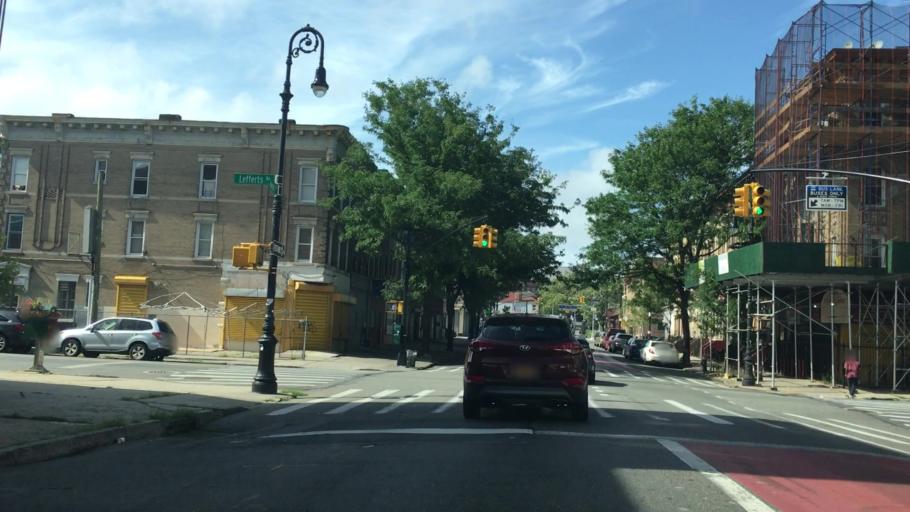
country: US
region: New York
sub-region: Kings County
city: Brooklyn
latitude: 40.6620
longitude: -73.9537
